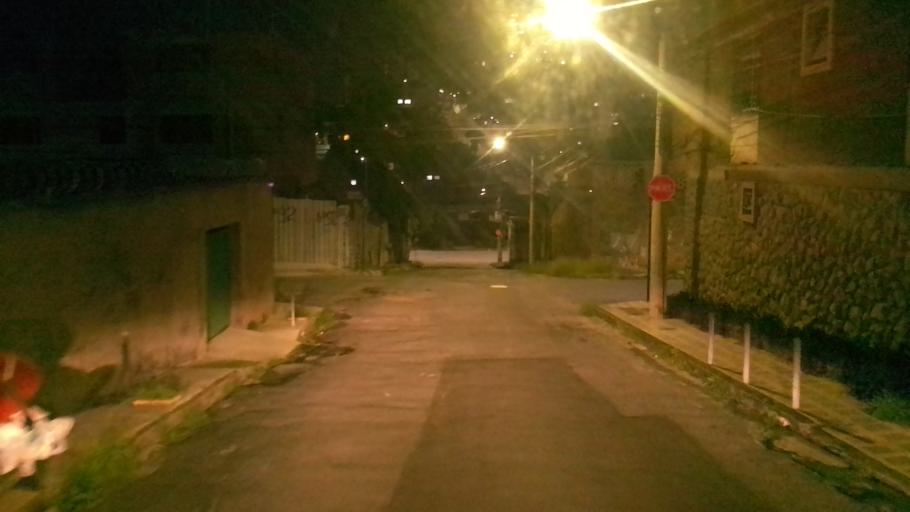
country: BR
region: Minas Gerais
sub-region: Belo Horizonte
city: Belo Horizonte
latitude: -19.9004
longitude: -43.9216
